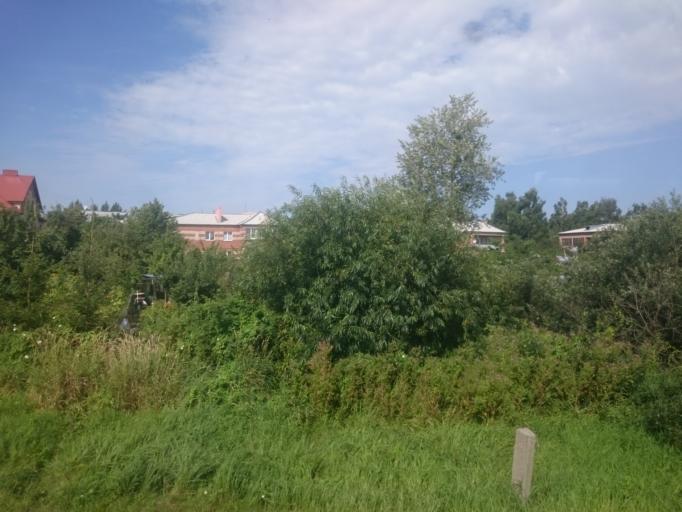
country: RU
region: Kaliningrad
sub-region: Zelenogradskiy Rayon
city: Zelenogradsk
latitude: 54.9545
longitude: 20.4725
